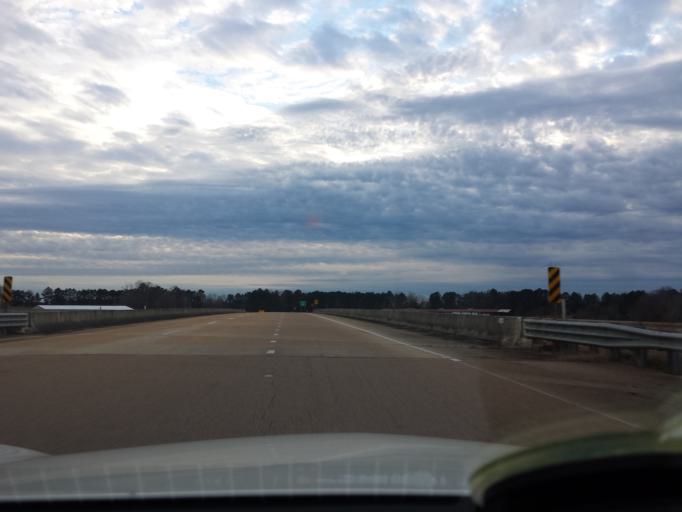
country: US
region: Mississippi
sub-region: Winston County
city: Louisville
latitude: 33.1578
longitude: -89.0868
